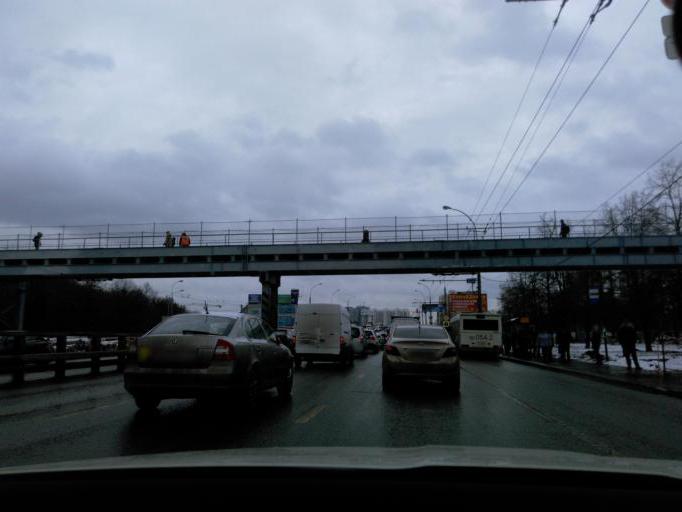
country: RU
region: Moscow
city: Likhobory
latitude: 55.8411
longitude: 37.5701
